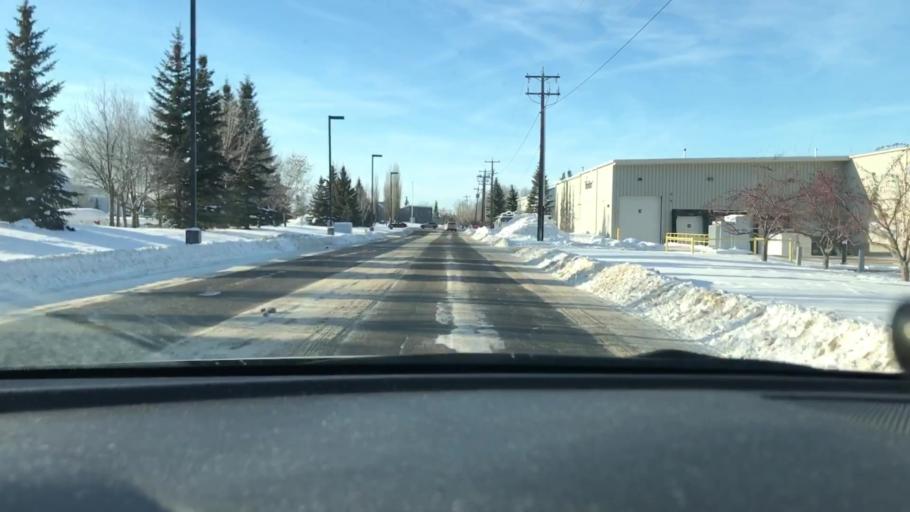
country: CA
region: Alberta
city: Edmonton
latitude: 53.4540
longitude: -113.4762
